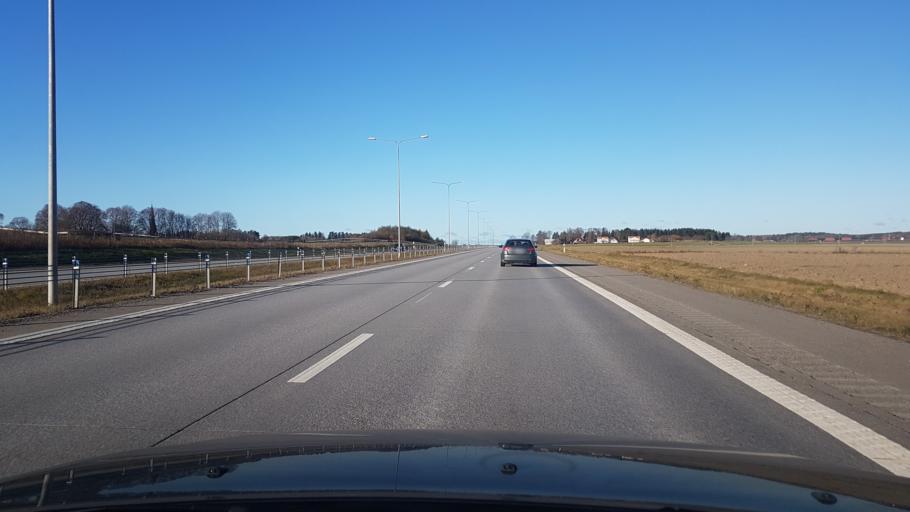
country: SE
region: Uppsala
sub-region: Uppsala Kommun
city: Saevja
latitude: 59.8720
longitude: 17.7024
